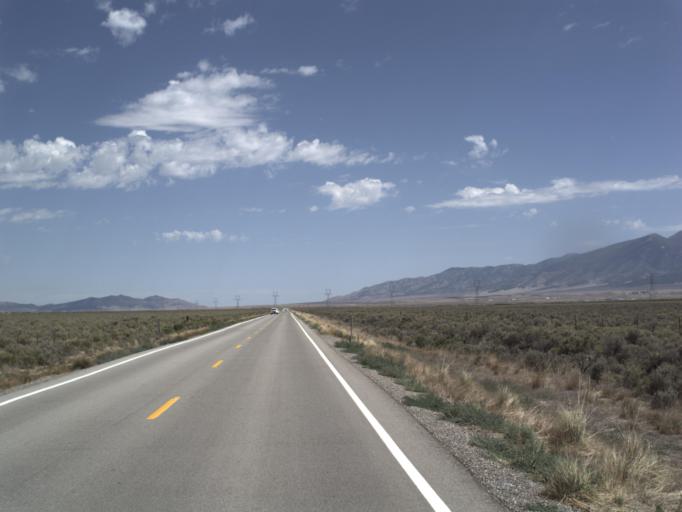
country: US
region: Utah
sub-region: Tooele County
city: Tooele
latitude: 40.2346
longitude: -112.4025
